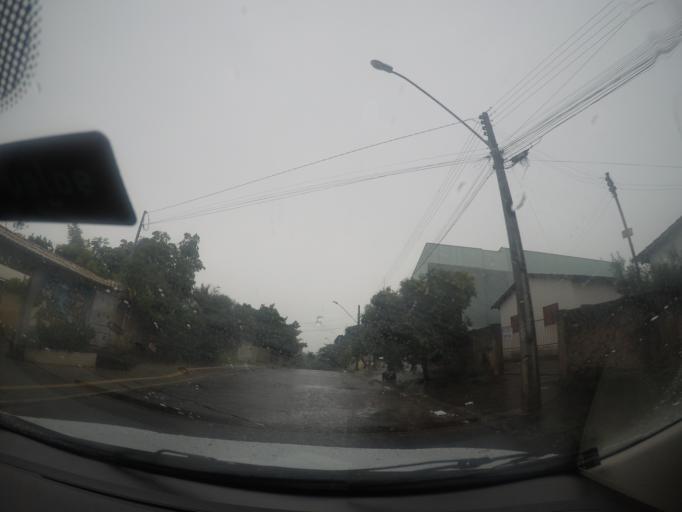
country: BR
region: Goias
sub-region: Goiania
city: Goiania
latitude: -16.6581
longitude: -49.3123
